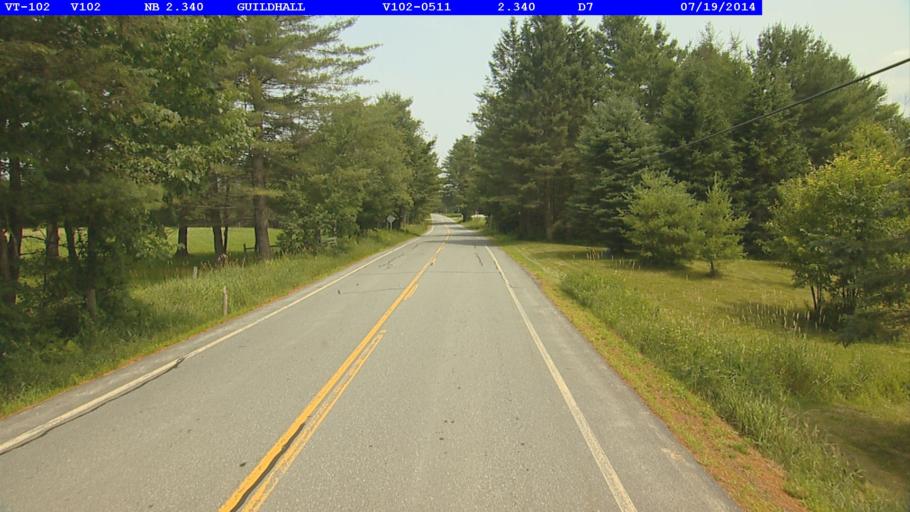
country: US
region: New Hampshire
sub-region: Coos County
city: Lancaster
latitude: 44.5276
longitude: -71.5900
